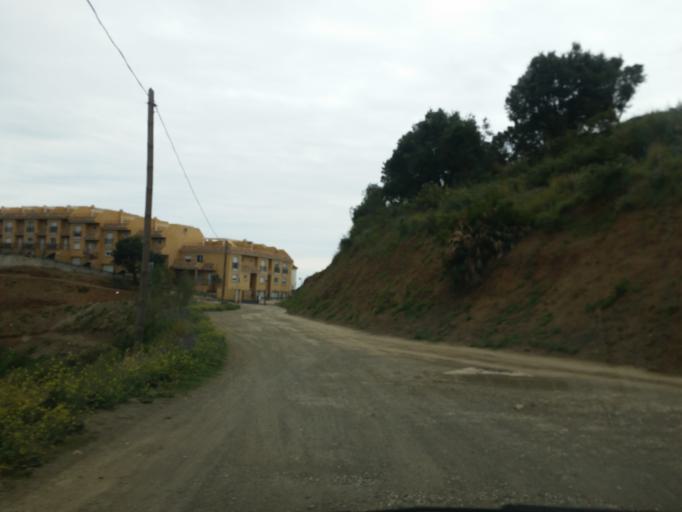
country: ES
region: Andalusia
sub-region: Provincia de Malaga
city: Mijas
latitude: 36.5785
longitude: -4.6083
